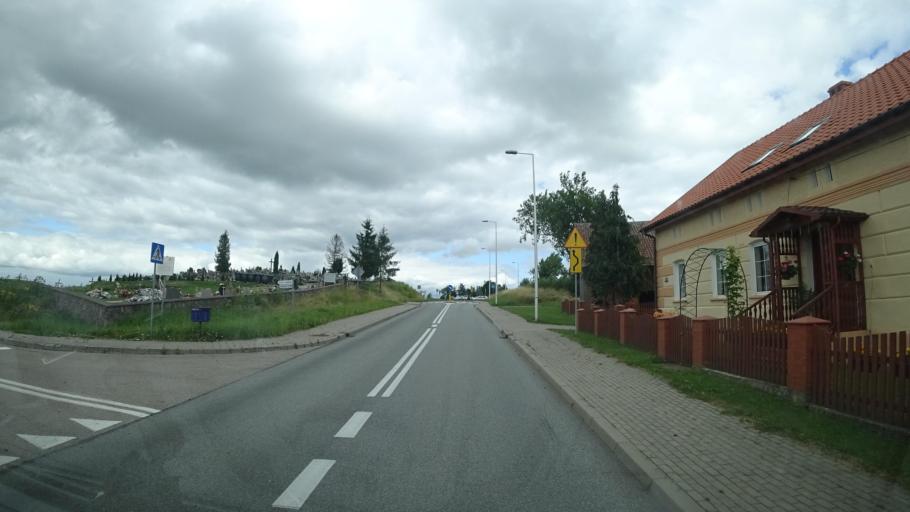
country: PL
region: Warmian-Masurian Voivodeship
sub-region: Powiat goldapski
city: Goldap
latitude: 54.2275
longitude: 22.2439
